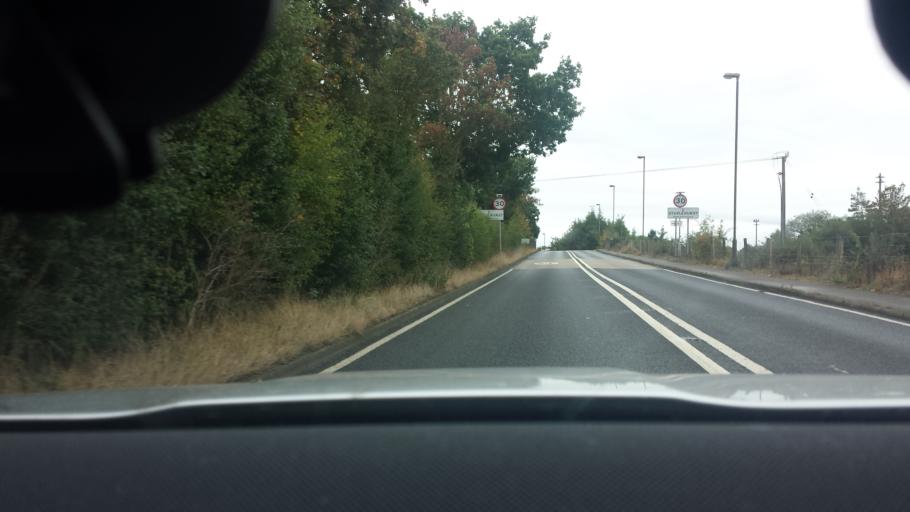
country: GB
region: England
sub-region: Kent
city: Staplehurst
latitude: 51.1725
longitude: 0.5525
